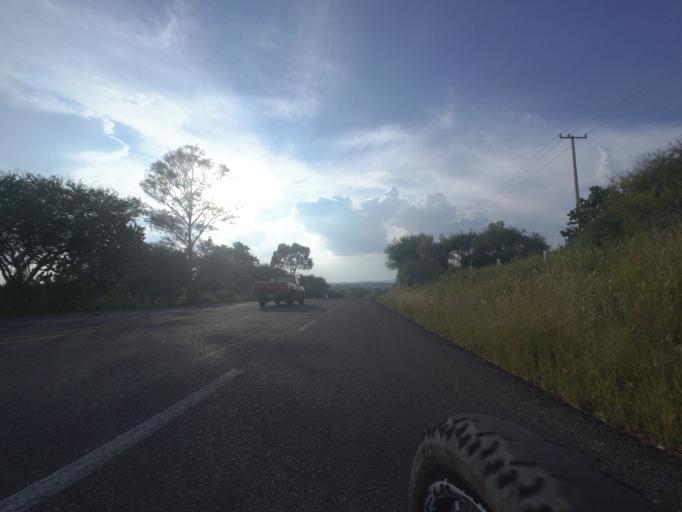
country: MX
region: Aguascalientes
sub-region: Aguascalientes
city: Penuelas (El Cienegal)
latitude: 21.7667
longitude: -102.3558
